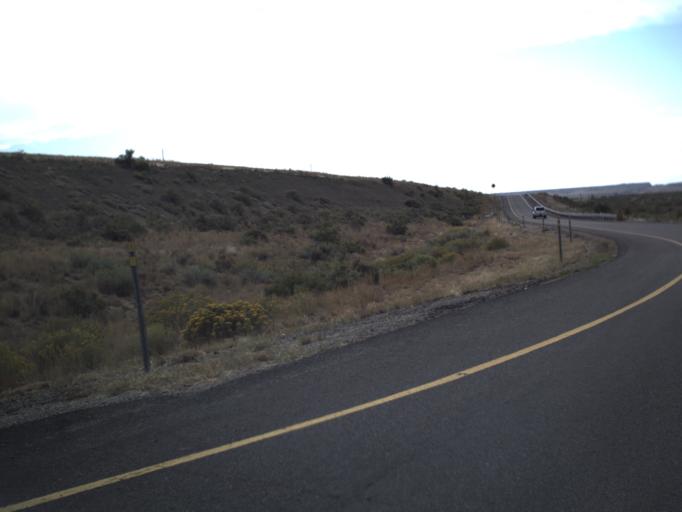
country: US
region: Utah
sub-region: Grand County
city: Moab
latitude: 38.9629
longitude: -109.7226
